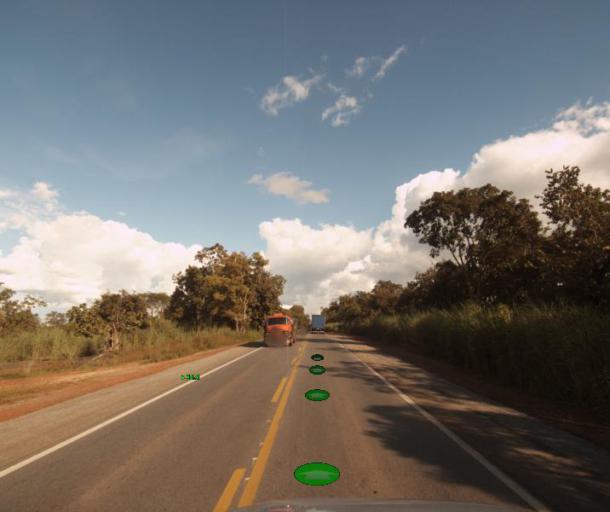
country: BR
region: Goias
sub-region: Porangatu
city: Porangatu
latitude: -13.1267
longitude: -49.1961
